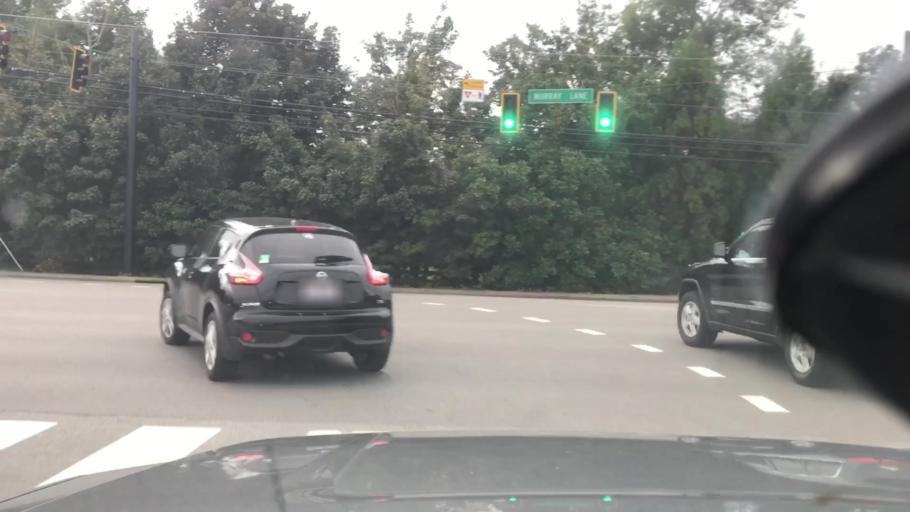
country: US
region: Tennessee
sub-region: Williamson County
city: Brentwood
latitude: 36.0153
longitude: -86.8143
